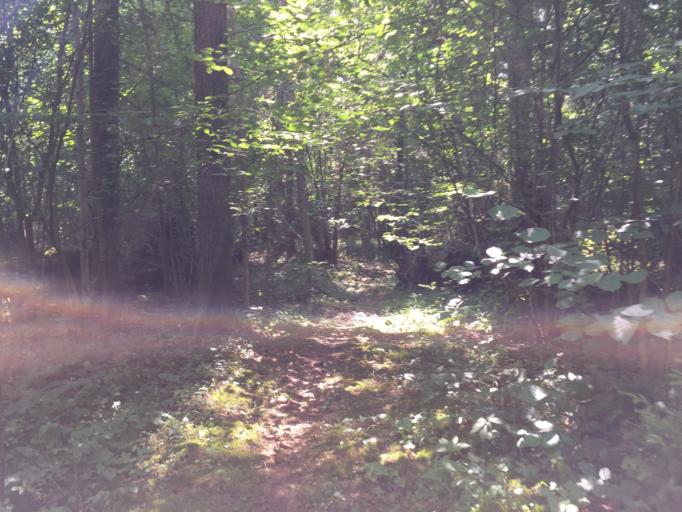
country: LT
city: Zagare
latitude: 56.3832
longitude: 23.2065
